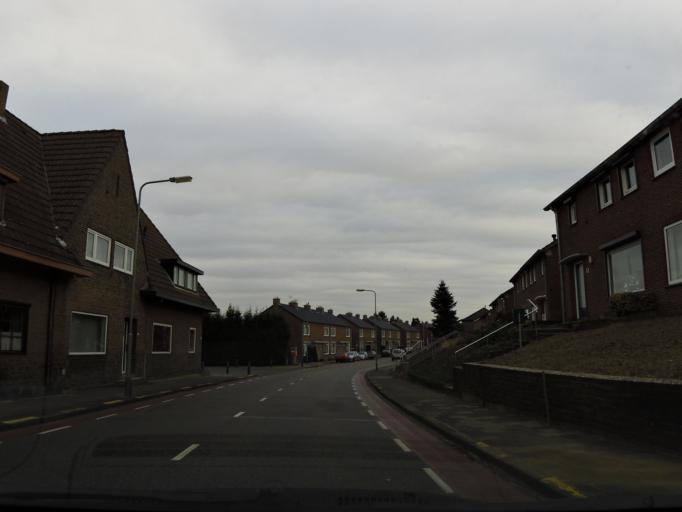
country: NL
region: Limburg
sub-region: Gemeente Schinnen
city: Schinnen
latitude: 50.9431
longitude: 5.8920
